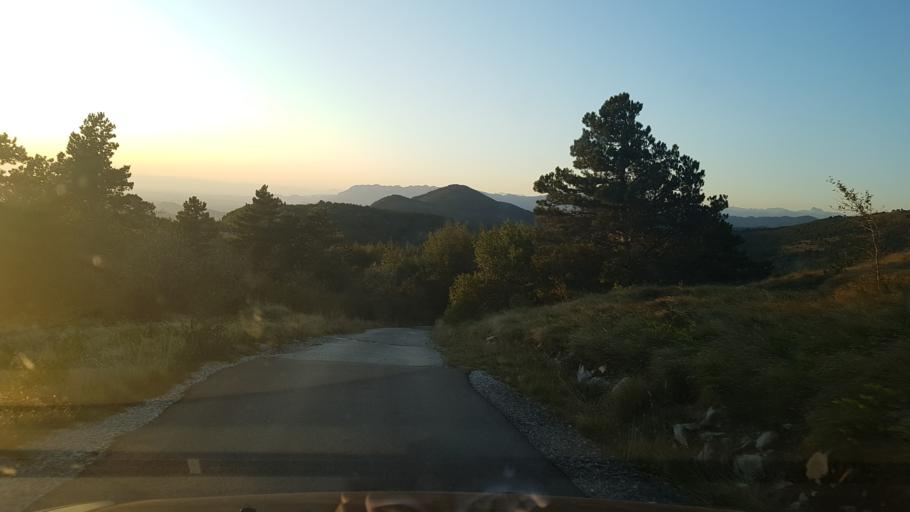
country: SI
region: Vipava
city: Vipava
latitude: 45.7855
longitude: 14.0260
